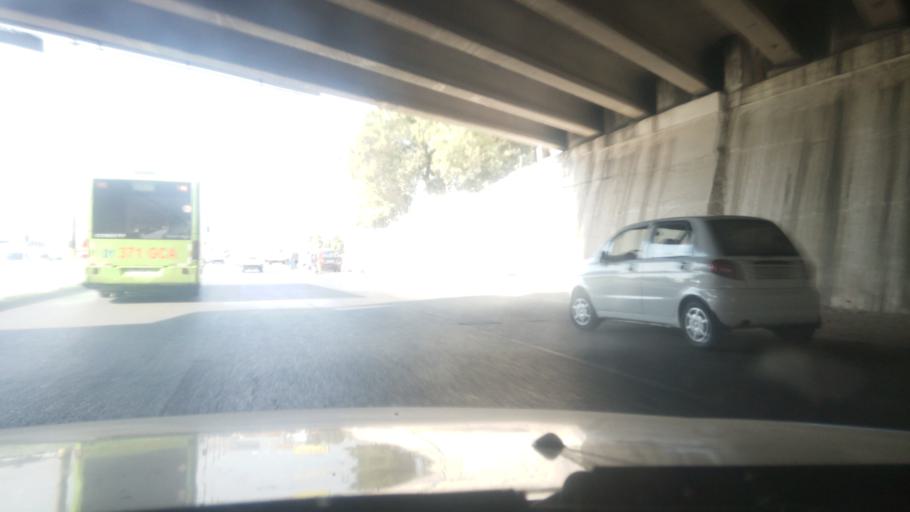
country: UZ
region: Toshkent Shahri
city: Tashkent
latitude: 41.2386
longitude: 69.1678
